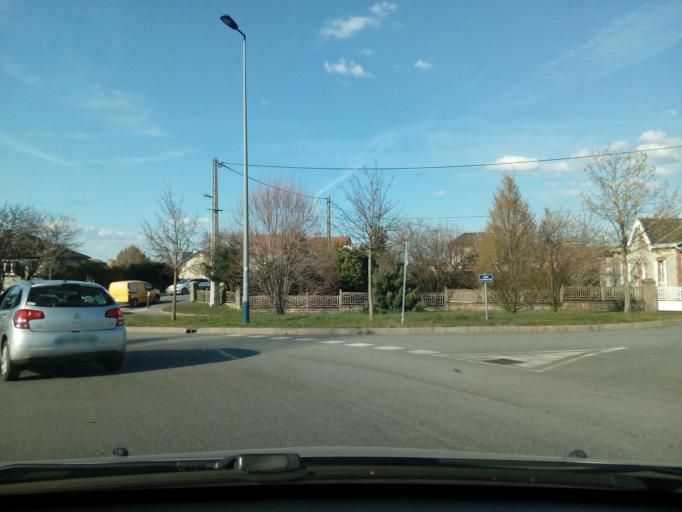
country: FR
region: Limousin
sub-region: Departement de la Creuse
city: Gueret
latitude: 46.1722
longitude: 1.8844
